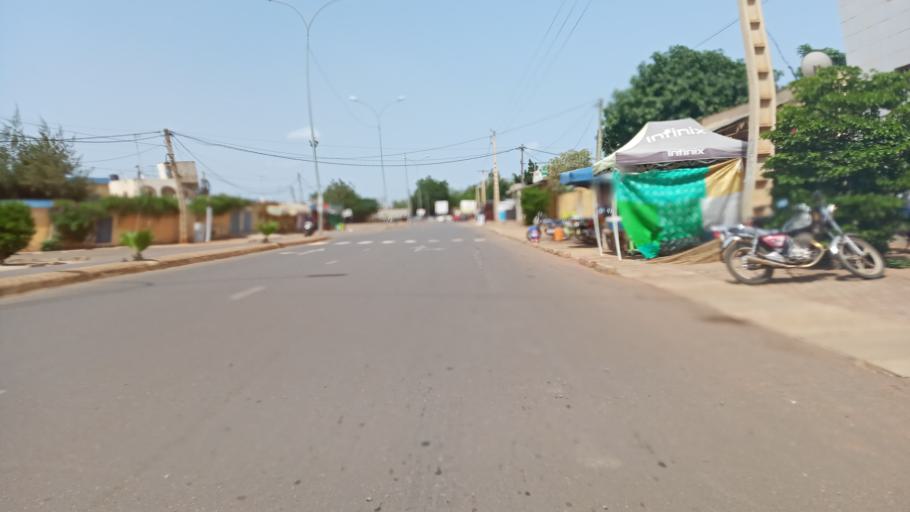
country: TG
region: Maritime
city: Lome
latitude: 6.2263
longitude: 1.2017
